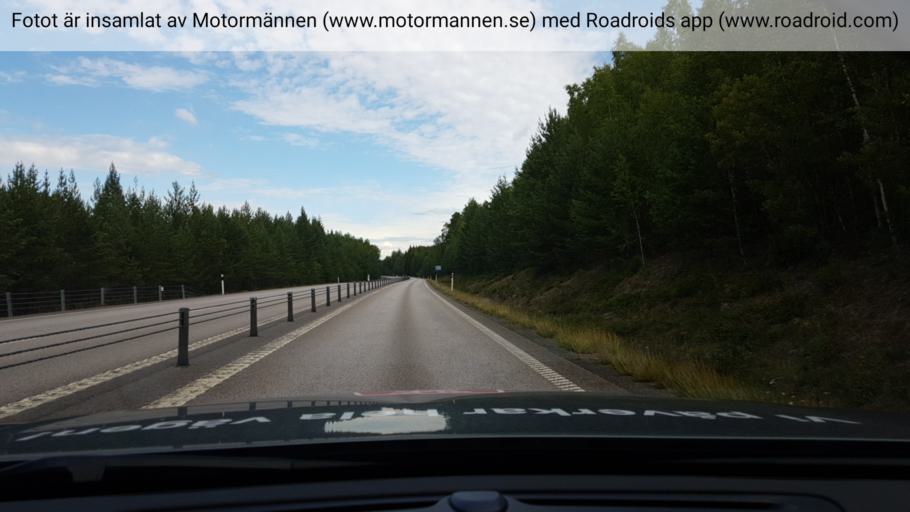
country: SE
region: Uppsala
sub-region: Heby Kommun
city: Tarnsjo
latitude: 60.2784
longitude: 16.9306
